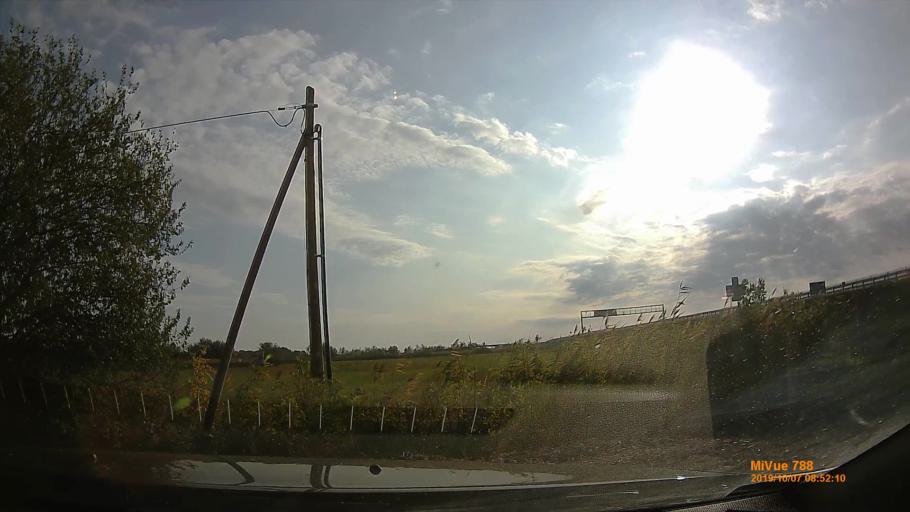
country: HU
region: Bekes
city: Szarvas
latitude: 46.8182
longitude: 20.5253
